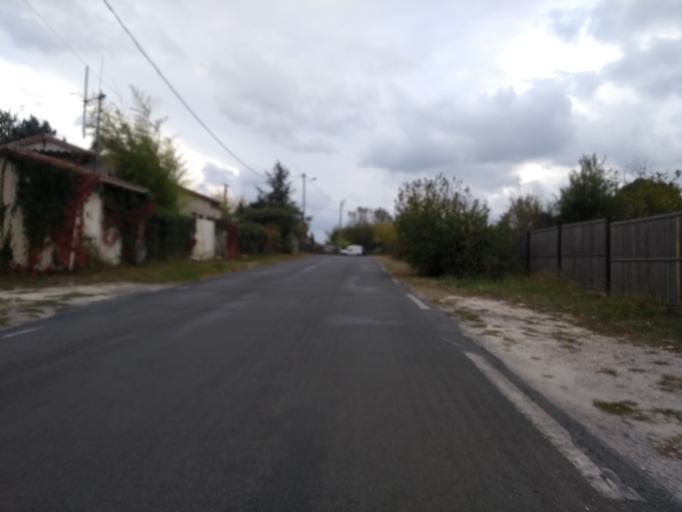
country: FR
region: Aquitaine
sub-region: Departement de la Gironde
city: Pessac
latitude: 44.8169
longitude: -0.6588
